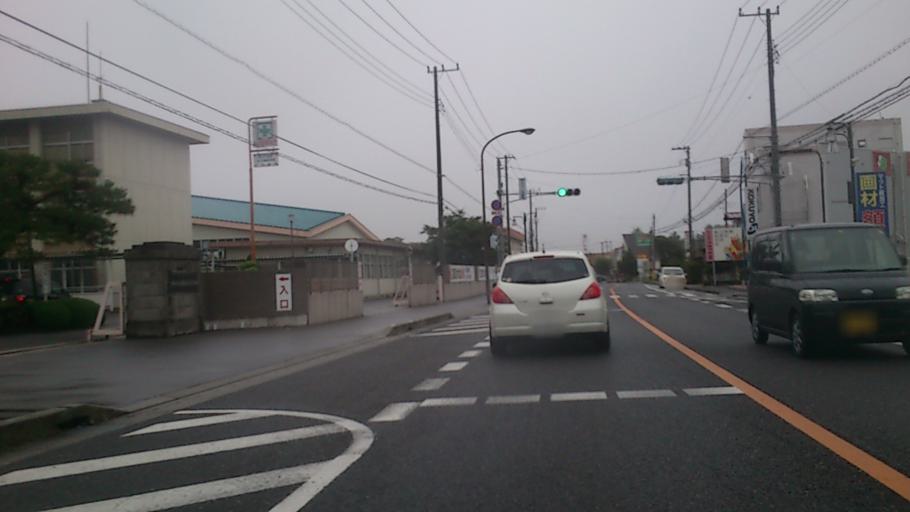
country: JP
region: Tochigi
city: Otawara
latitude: 36.8620
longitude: 140.0322
